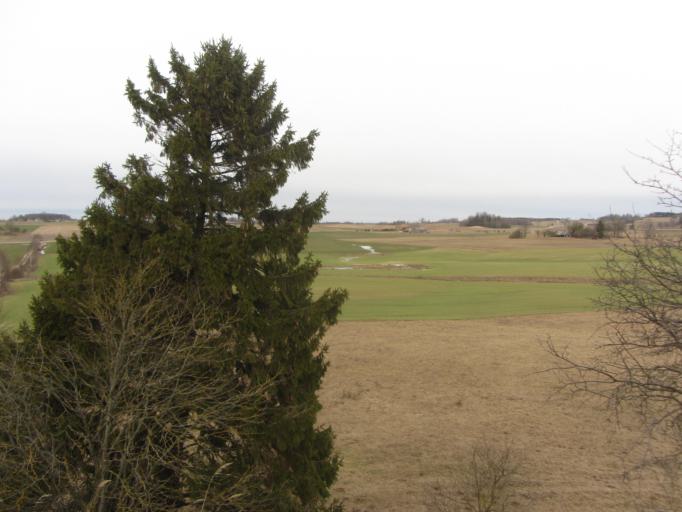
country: LT
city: Prienai
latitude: 54.6239
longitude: 23.7461
